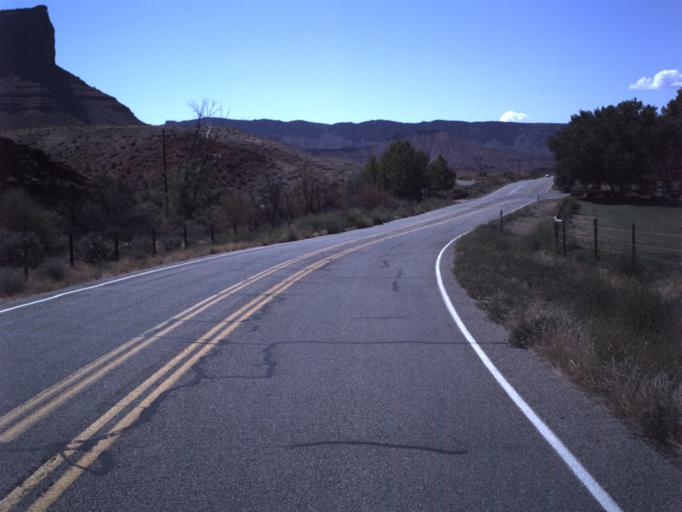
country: US
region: Utah
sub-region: Grand County
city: Moab
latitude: 38.6992
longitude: -109.3957
